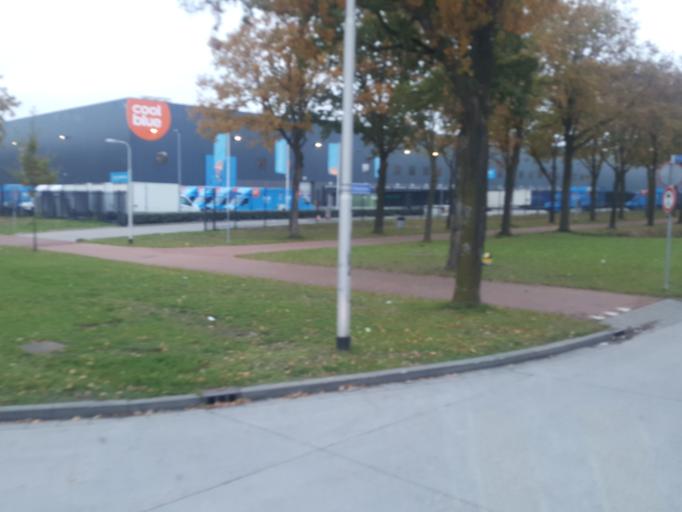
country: NL
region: North Brabant
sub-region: Gemeente Dongen
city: Dongen
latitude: 51.6013
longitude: 4.9970
